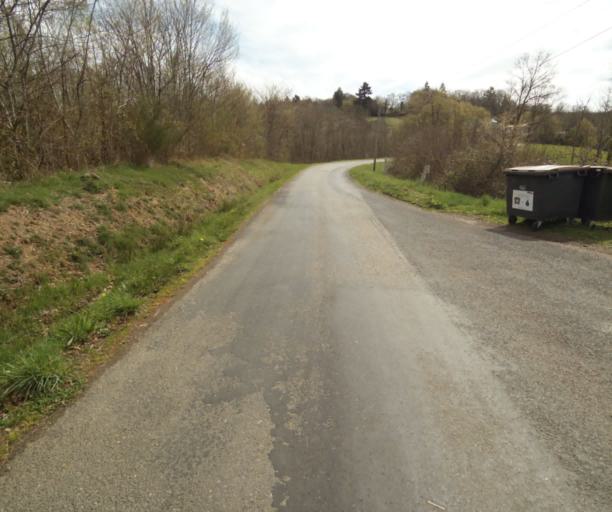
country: FR
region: Limousin
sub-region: Departement de la Correze
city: Laguenne
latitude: 45.2383
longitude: 1.8559
